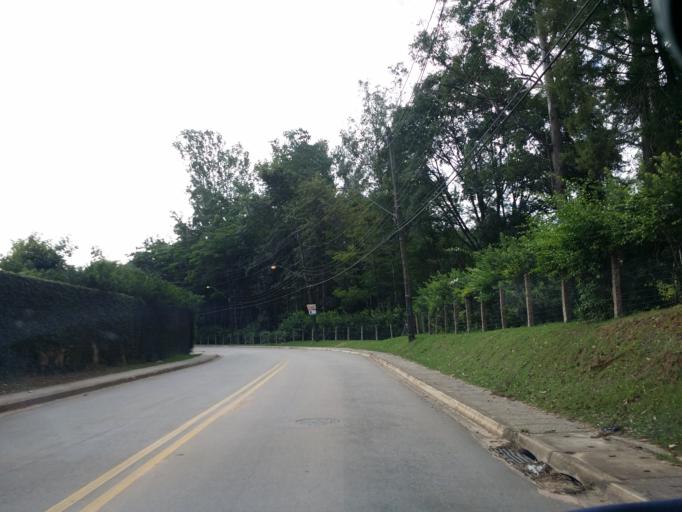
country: BR
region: Sao Paulo
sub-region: Itupeva
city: Itupeva
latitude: -23.1960
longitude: -47.0223
